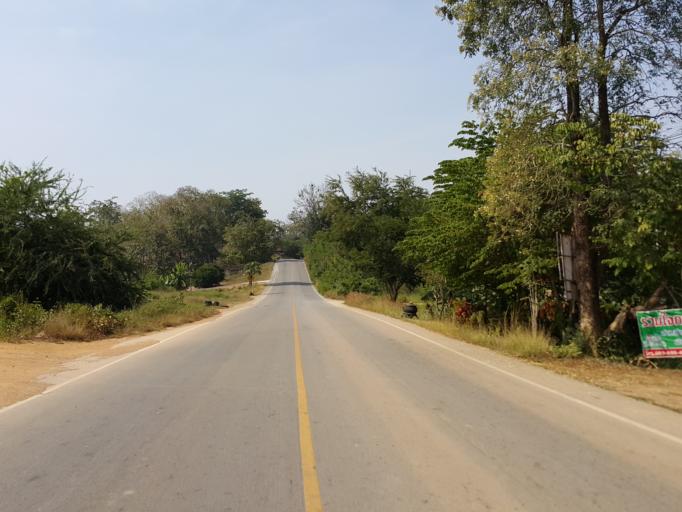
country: TH
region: Sukhothai
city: Thung Saliam
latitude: 17.3355
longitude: 99.4795
